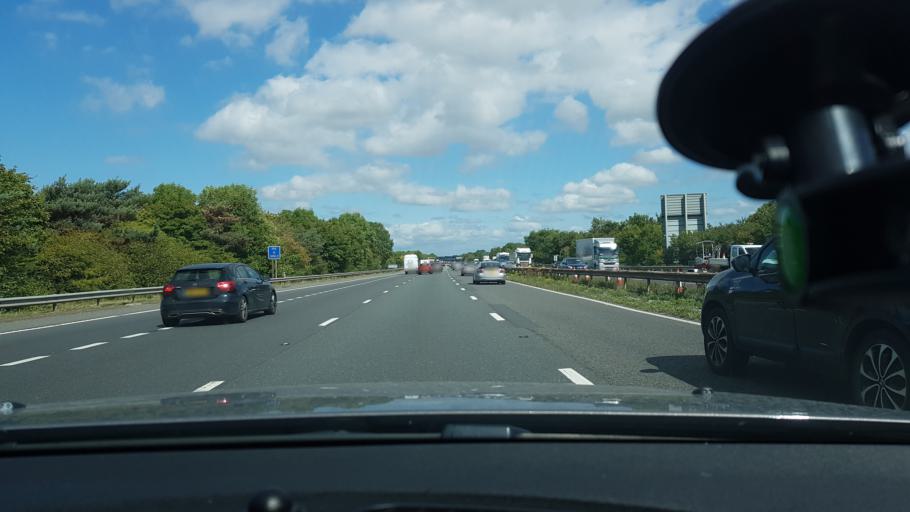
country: GB
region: England
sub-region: Somerset
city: Creech Saint Michael
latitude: 51.0210
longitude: -3.0603
